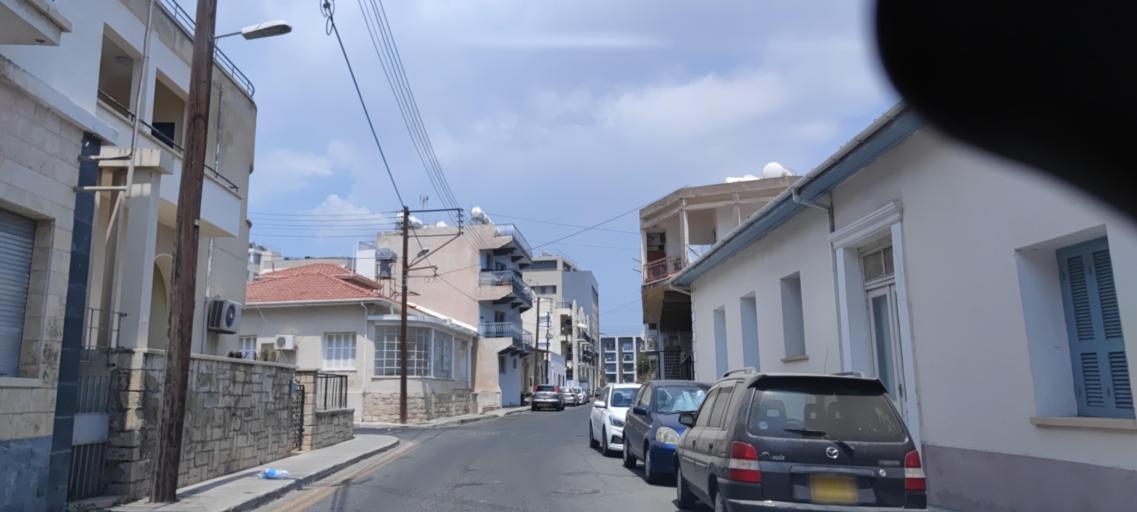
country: CY
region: Limassol
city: Limassol
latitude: 34.6806
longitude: 33.0472
